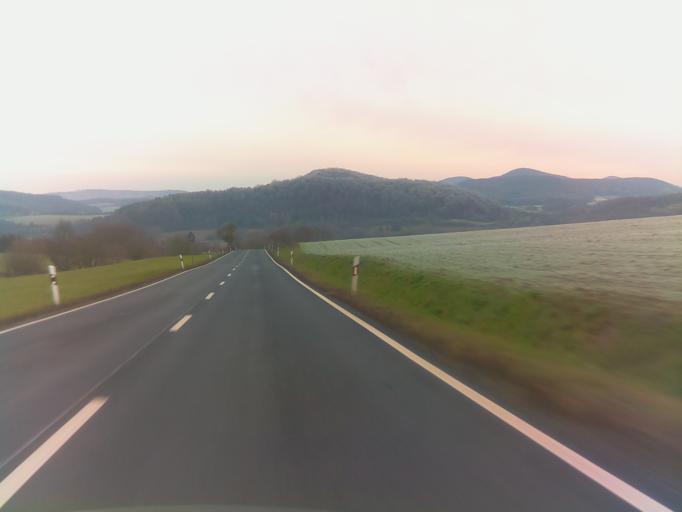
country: DE
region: Thuringia
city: Buttlar
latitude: 50.7704
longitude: 9.9659
